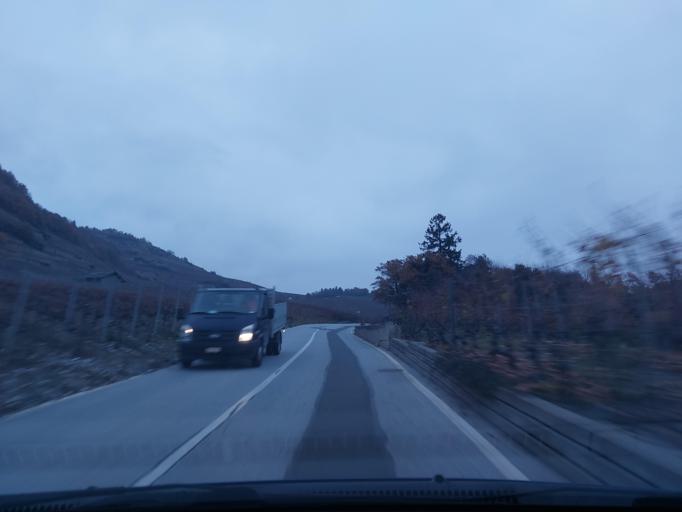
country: CH
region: Valais
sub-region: Sion District
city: Saviese
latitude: 46.2380
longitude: 7.3255
